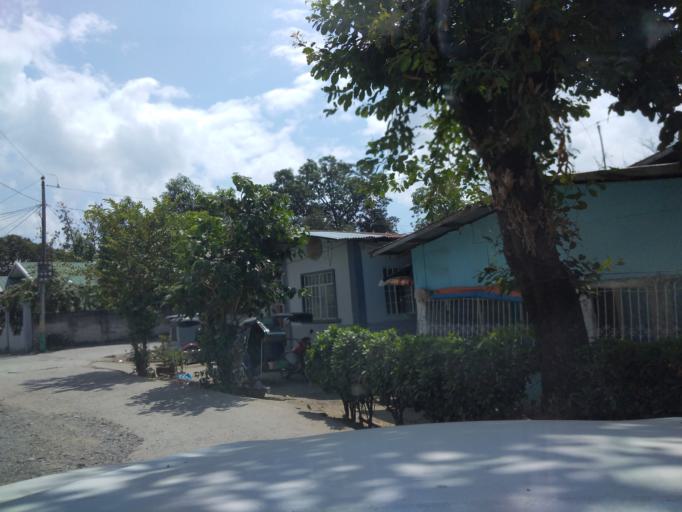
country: PH
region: Central Luzon
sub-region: Province of Pampanga
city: Lourdes
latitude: 15.0180
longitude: 120.8546
